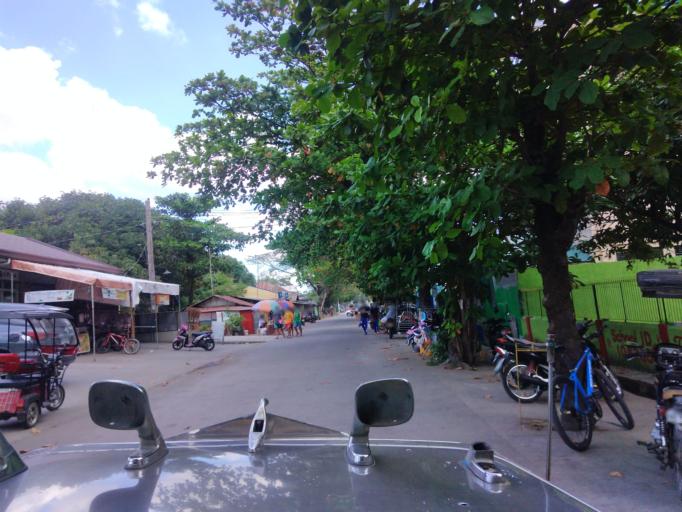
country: PH
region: Central Luzon
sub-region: Province of Pampanga
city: Santa Rita
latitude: 15.0078
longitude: 120.5925
